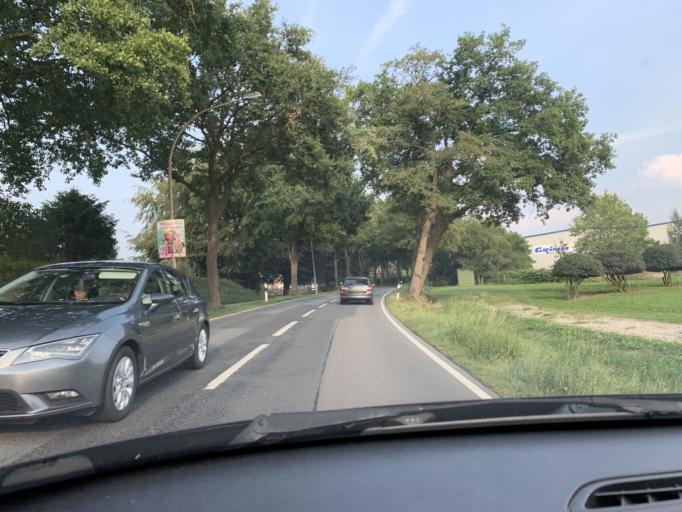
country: DE
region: Lower Saxony
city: Barssel
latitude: 53.1767
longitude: 7.7609
